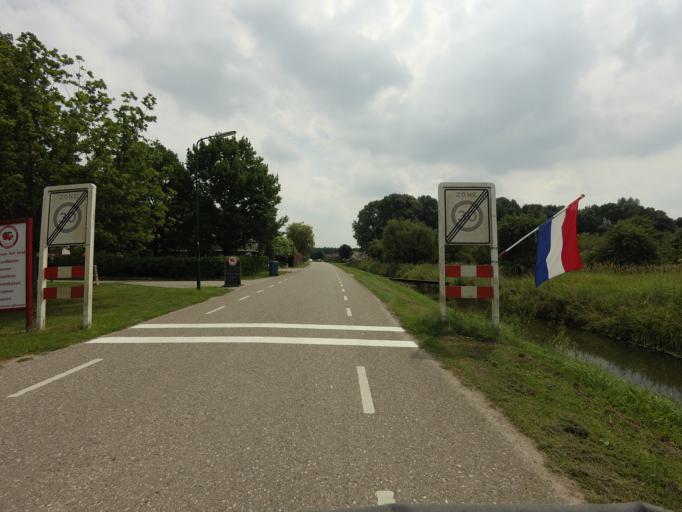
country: NL
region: Utrecht
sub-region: Gemeente Houten
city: Houten
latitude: 52.0000
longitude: 5.1385
